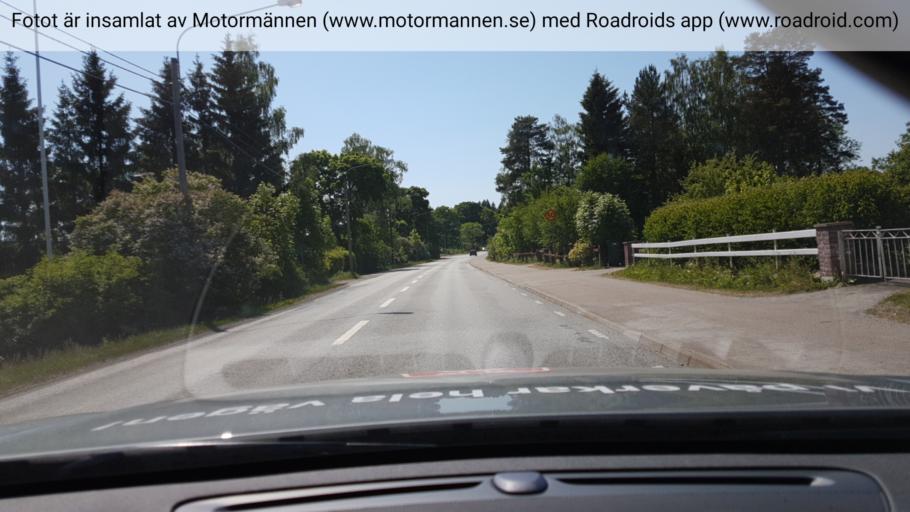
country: SE
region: Stockholm
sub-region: Norrtalje Kommun
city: Norrtalje
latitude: 59.8977
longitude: 18.7042
